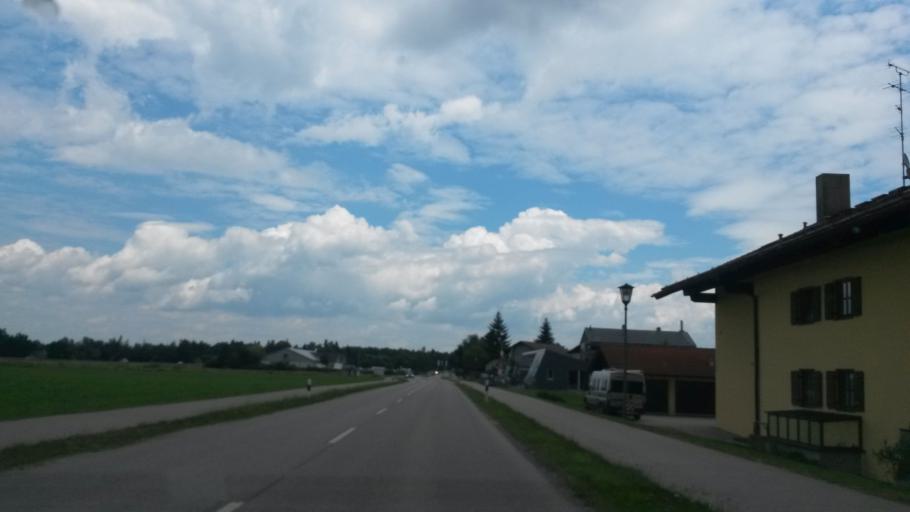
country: DE
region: Bavaria
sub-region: Upper Bavaria
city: Bernau am Chiemsee
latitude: 47.8218
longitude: 12.3825
